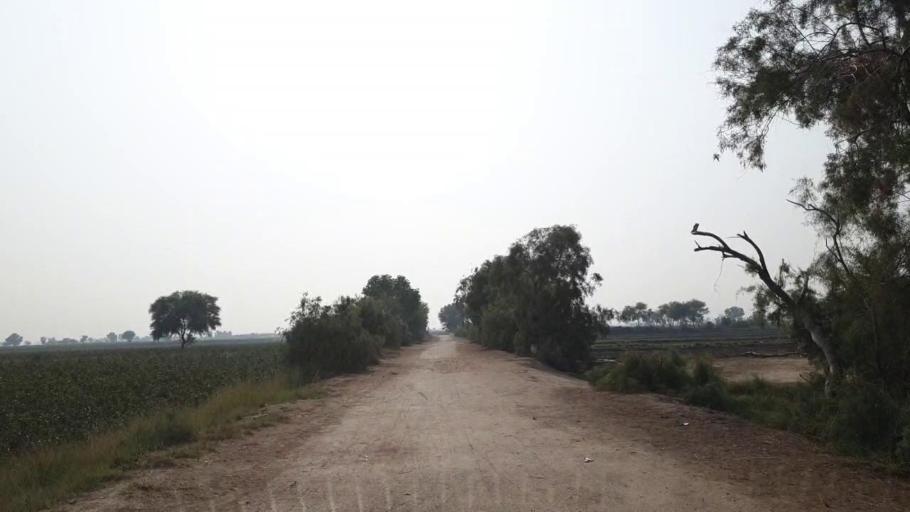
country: PK
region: Sindh
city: Bhan
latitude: 26.4662
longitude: 67.7392
